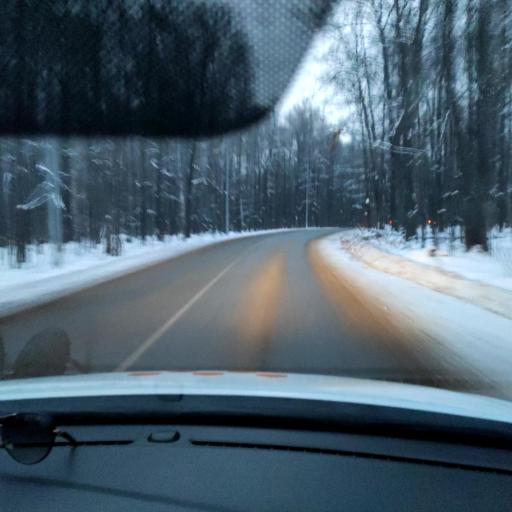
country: RU
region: Tatarstan
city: Vysokaya Gora
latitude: 55.9311
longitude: 49.1917
